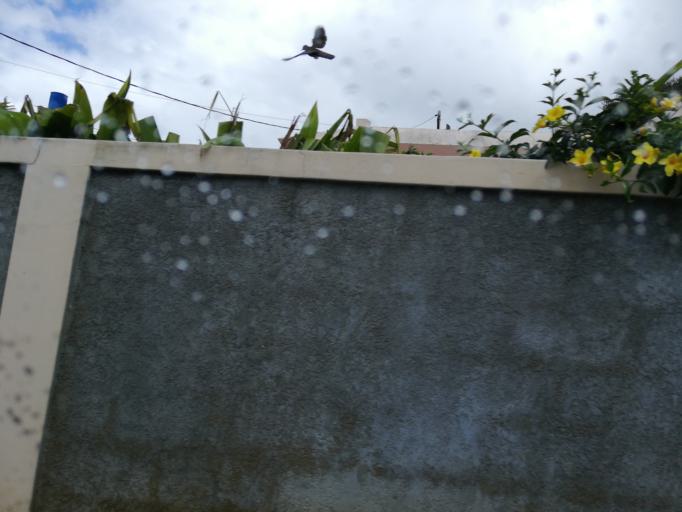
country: MU
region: Moka
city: Moka
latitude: -20.2176
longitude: 57.4720
